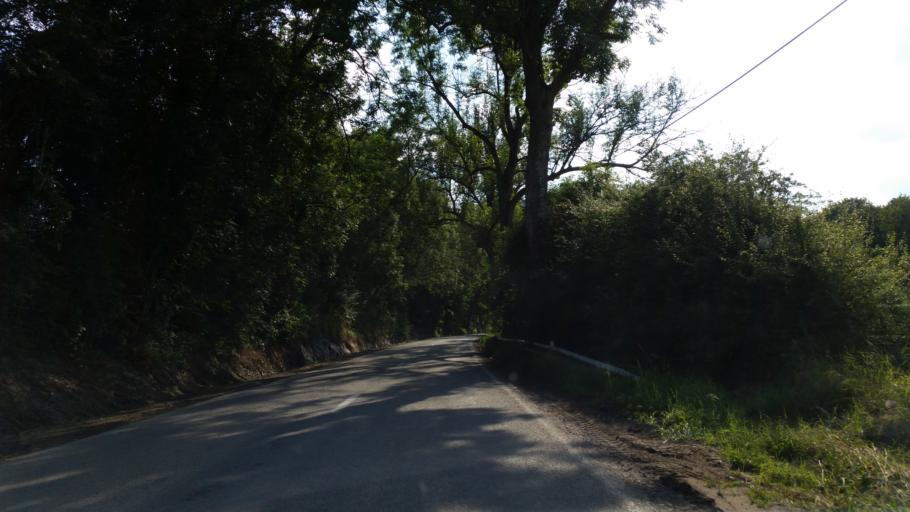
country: BE
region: Wallonia
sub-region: Province du Luxembourg
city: Durbuy
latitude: 50.3756
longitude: 5.4665
